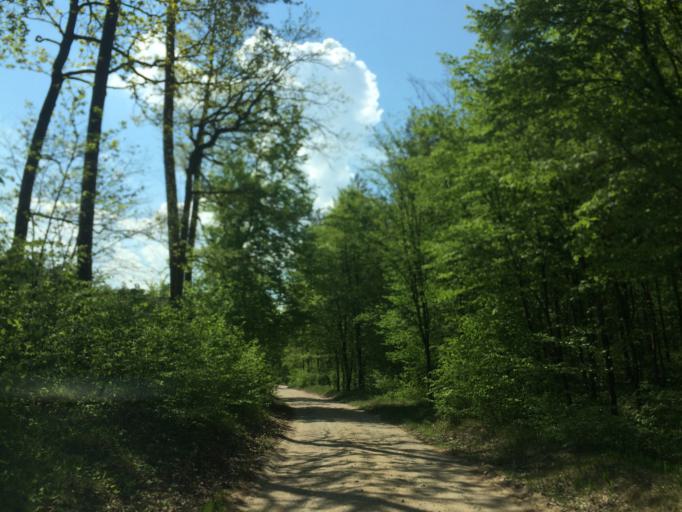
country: PL
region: Warmian-Masurian Voivodeship
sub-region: Powiat nowomiejski
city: Nowe Miasto Lubawskie
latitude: 53.4513
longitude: 19.6323
